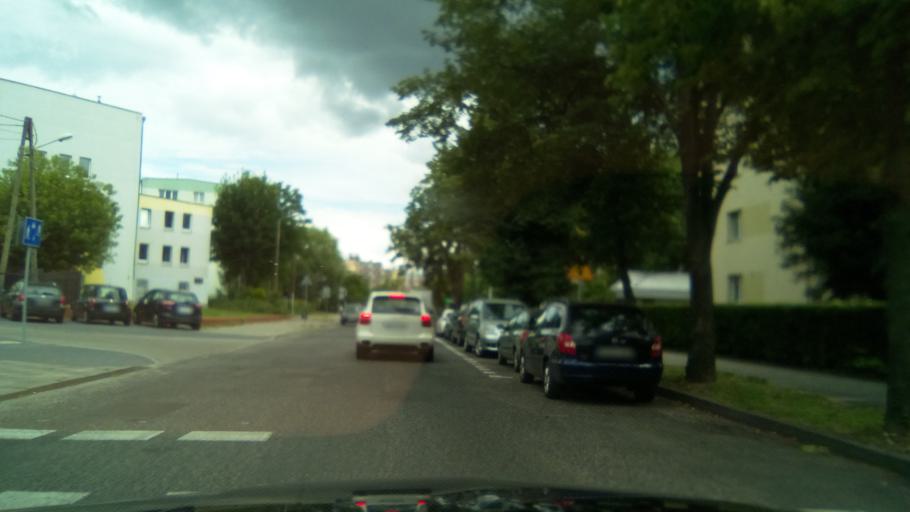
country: PL
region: Greater Poland Voivodeship
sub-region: Powiat gnieznienski
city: Gniezno
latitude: 52.5417
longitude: 17.6176
